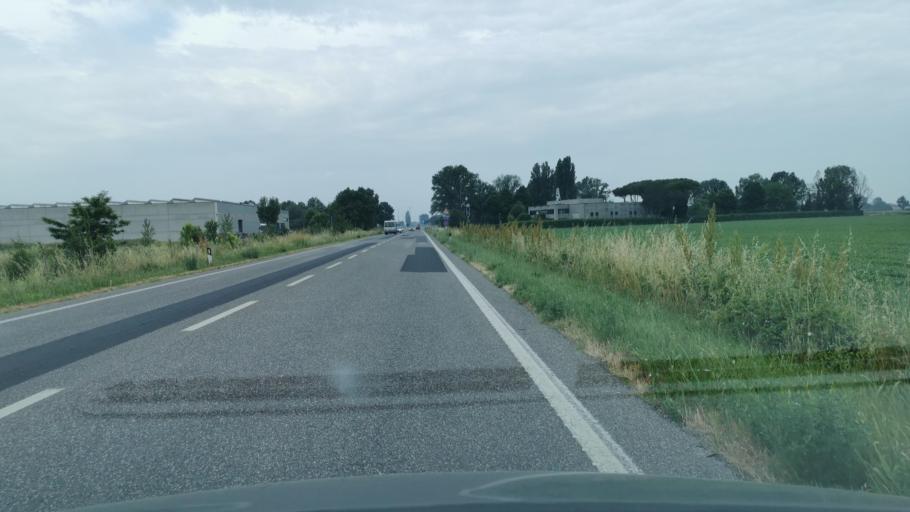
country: IT
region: Emilia-Romagna
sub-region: Provincia di Ravenna
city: Godo
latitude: 44.3957
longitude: 12.0728
